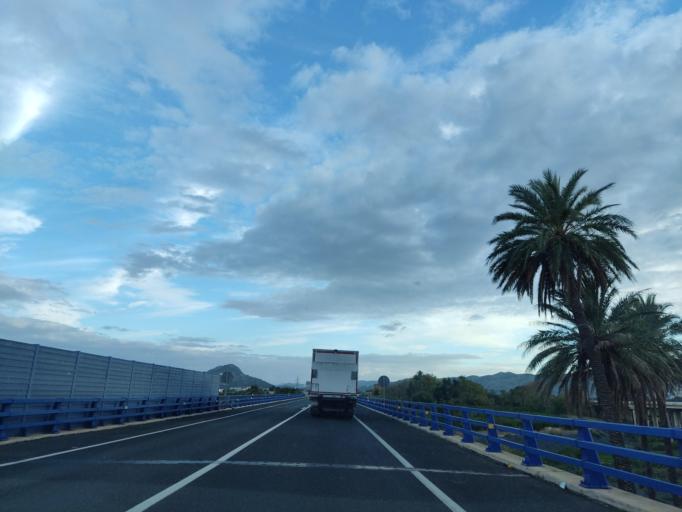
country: ES
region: Valencia
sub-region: Provincia de Alicante
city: Beniarbeig
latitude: 38.8287
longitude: 0.0059
